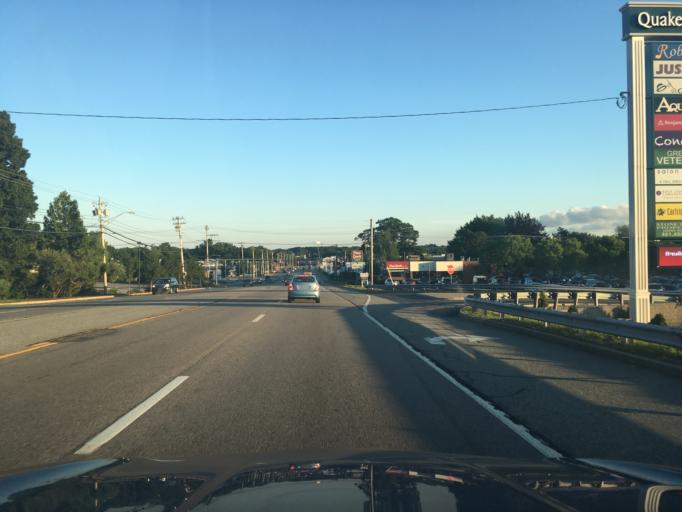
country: US
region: Rhode Island
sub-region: Kent County
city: West Warwick
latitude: 41.6753
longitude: -71.5000
